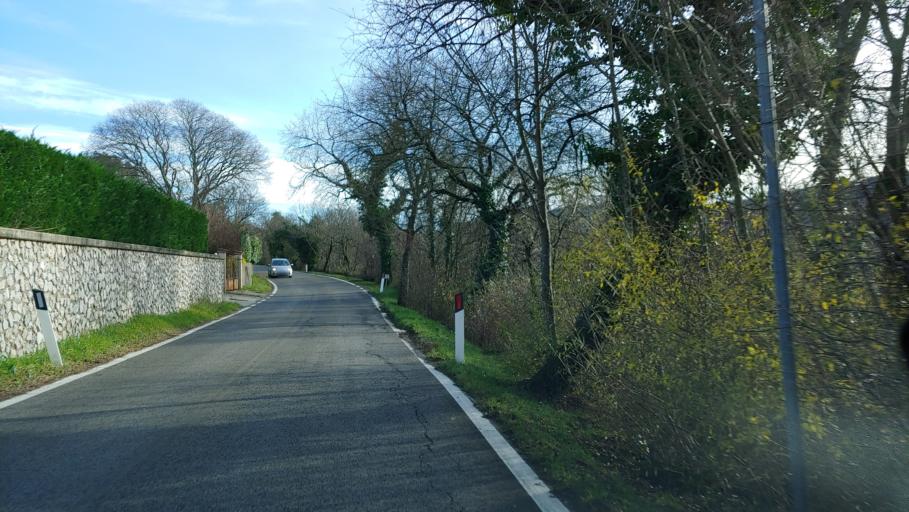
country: IT
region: Friuli Venezia Giulia
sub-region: Provincia di Trieste
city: Duino
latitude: 45.8160
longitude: 13.5913
